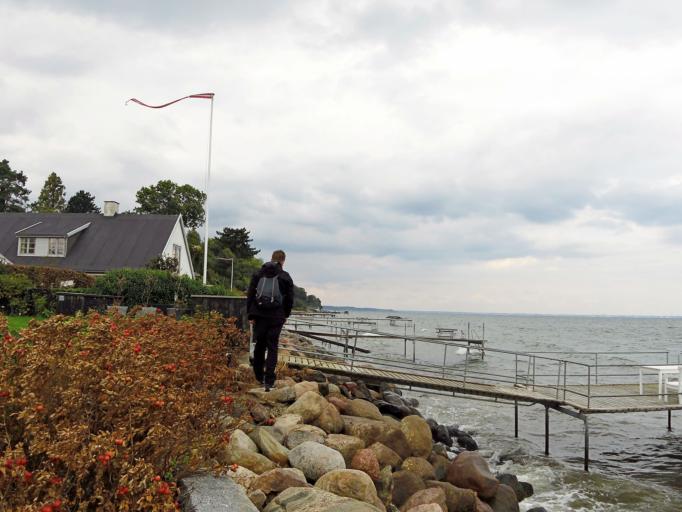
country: DK
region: Capital Region
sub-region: Fredensborg Kommune
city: Humlebaek
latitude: 55.9552
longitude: 12.5362
